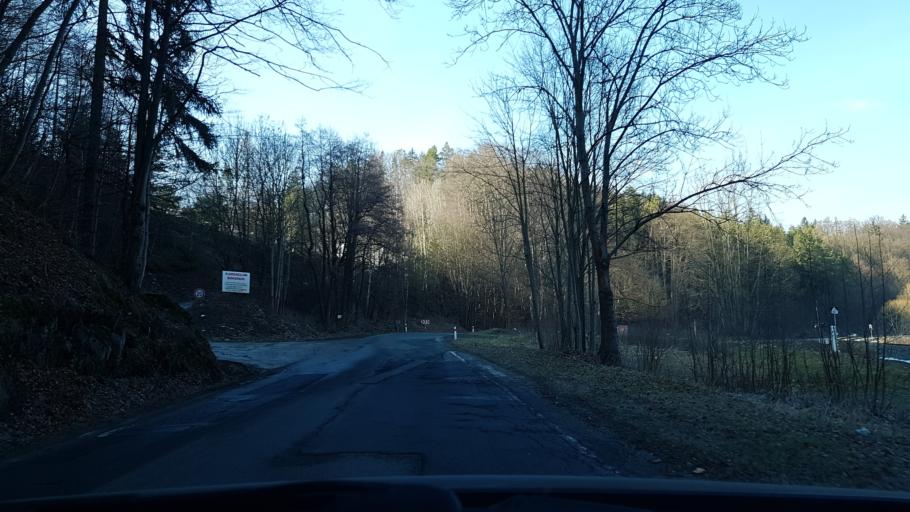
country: CZ
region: Olomoucky
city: Dolni Bohdikov
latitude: 50.0200
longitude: 16.8959
